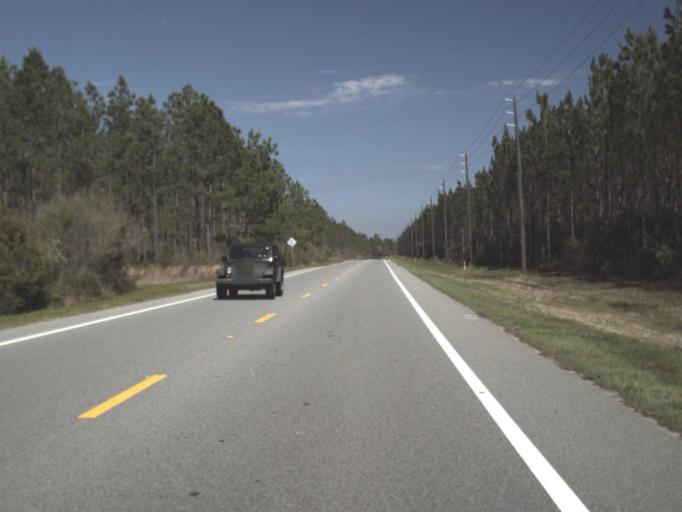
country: US
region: Florida
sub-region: Bay County
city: Panama City Beach
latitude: 30.3264
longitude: -85.7828
